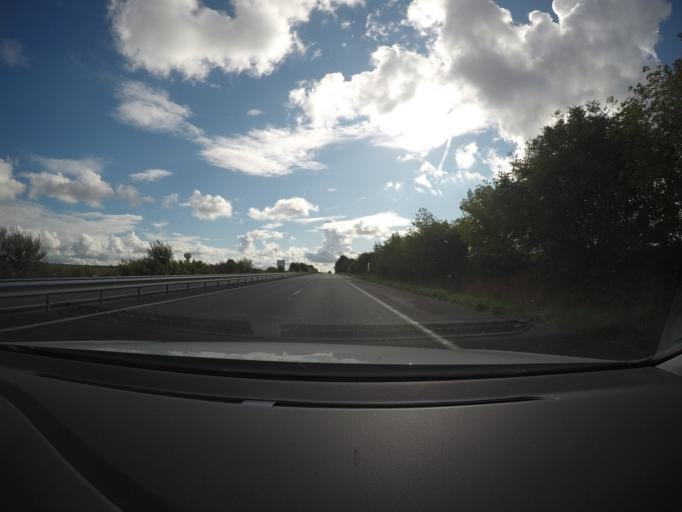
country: FR
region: Nord-Pas-de-Calais
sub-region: Departement du Pas-de-Calais
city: Hermies
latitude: 50.1139
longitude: 3.0775
